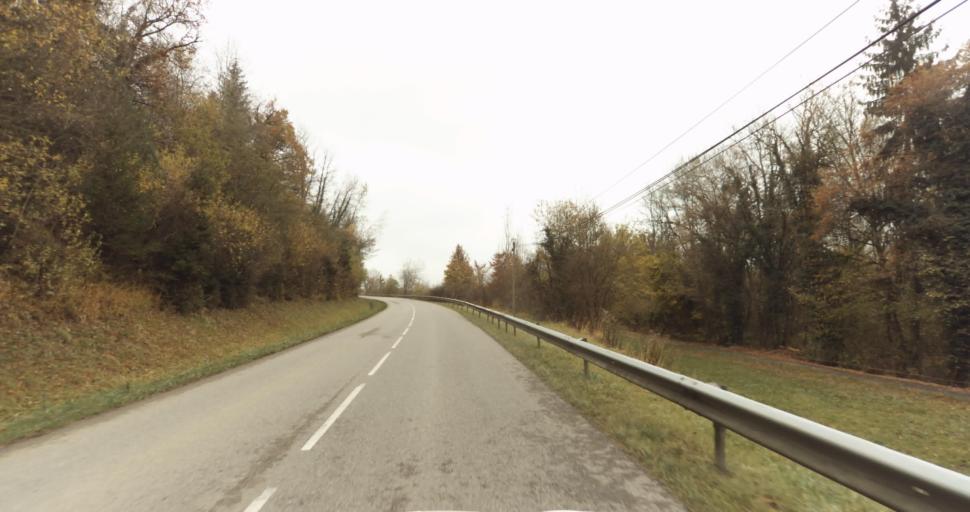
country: FR
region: Rhone-Alpes
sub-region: Departement de la Haute-Savoie
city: Viuz-la-Chiesaz
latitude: 45.8201
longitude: 6.0585
